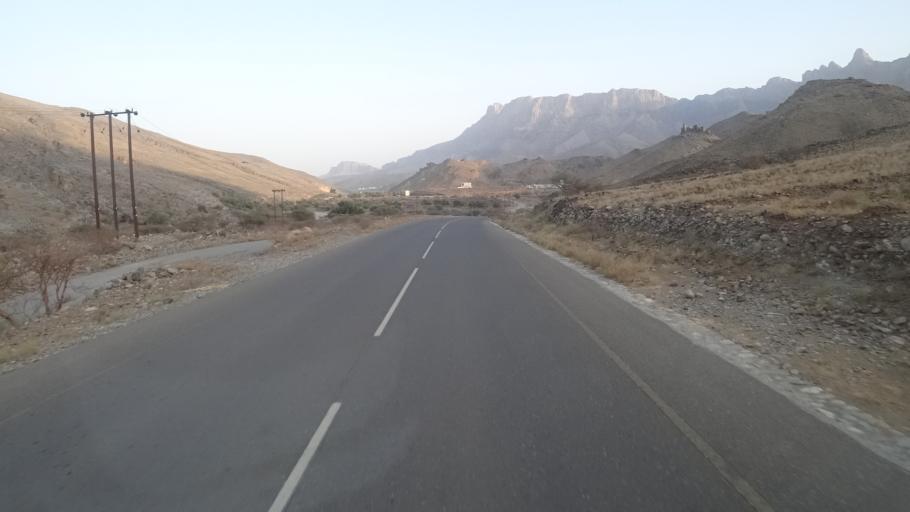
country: OM
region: Muhafazat ad Dakhiliyah
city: Bahla'
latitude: 23.1788
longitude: 57.1438
